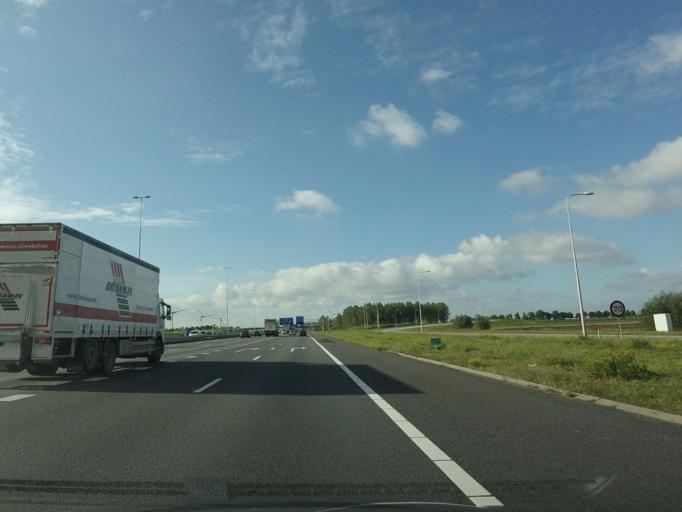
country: NL
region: South Holland
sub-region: Gemeente Kaag en Braassem
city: Leimuiden
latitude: 52.2431
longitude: 4.6618
